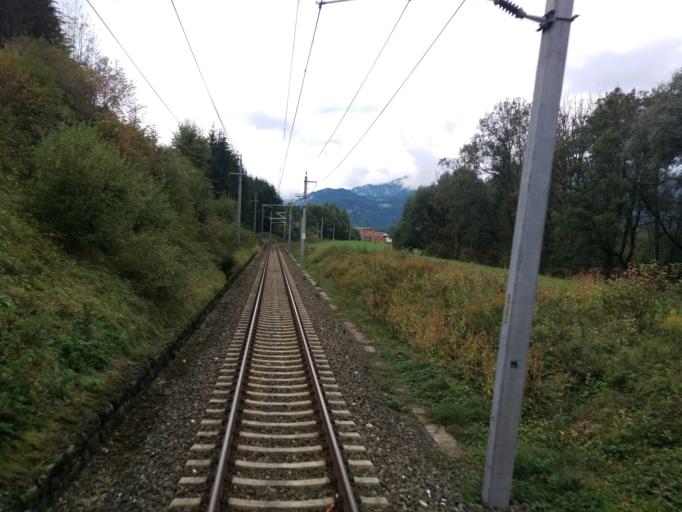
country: AT
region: Styria
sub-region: Politischer Bezirk Liezen
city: Liezen
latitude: 47.5506
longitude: 14.2626
